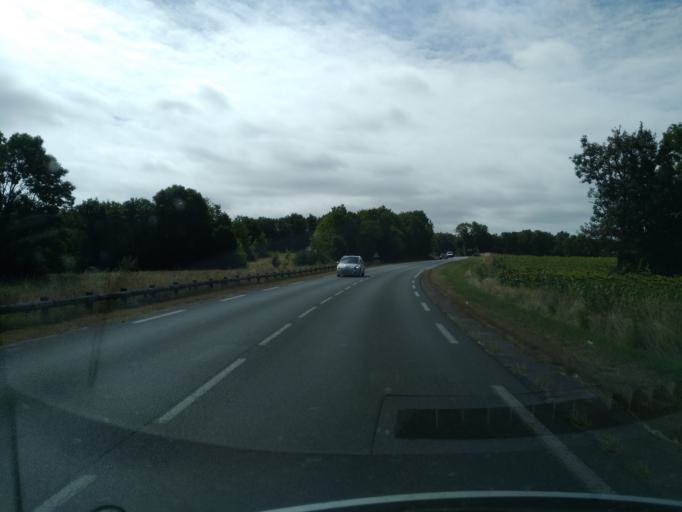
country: FR
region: Poitou-Charentes
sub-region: Departement de la Charente-Maritime
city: Breuillet
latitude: 45.7036
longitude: -1.0578
